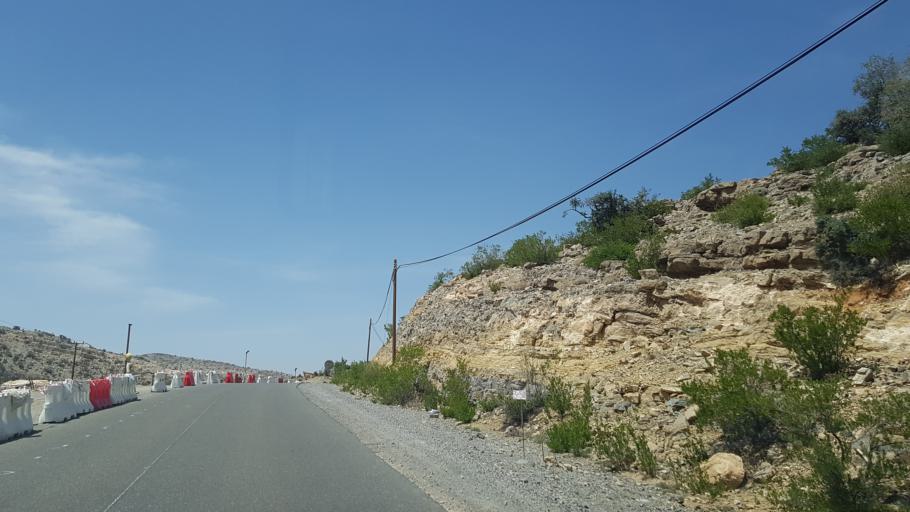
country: OM
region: Muhafazat ad Dakhiliyah
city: Izki
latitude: 23.1078
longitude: 57.6610
